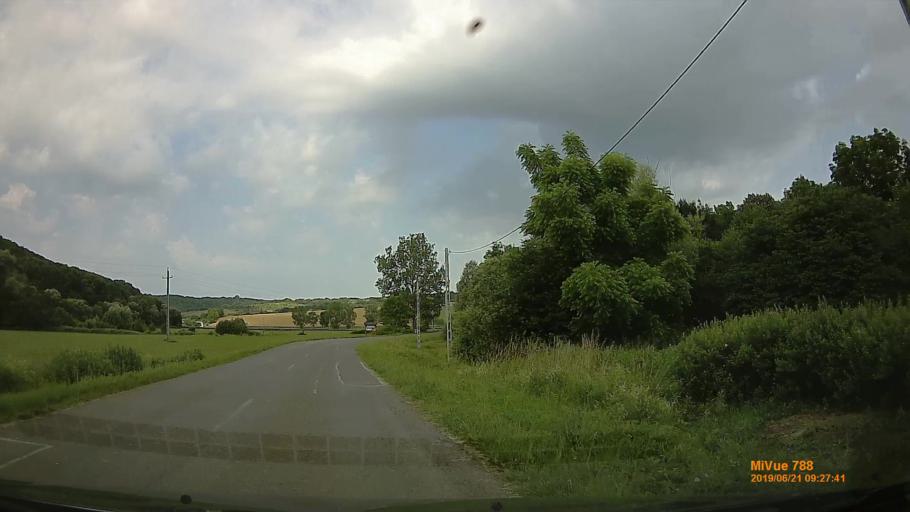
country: HU
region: Somogy
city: Taszar
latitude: 46.2787
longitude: 17.8949
